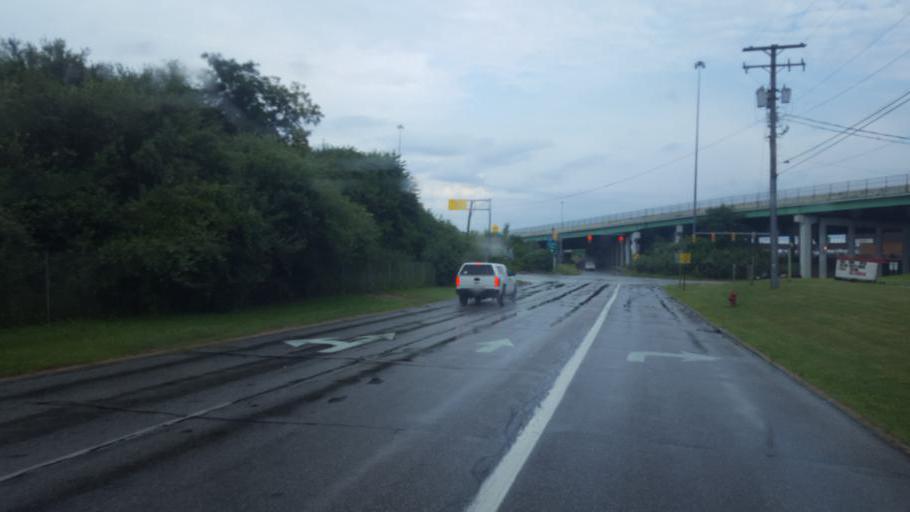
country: US
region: Ohio
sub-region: Cuyahoga County
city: Bedford Heights
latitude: 41.4230
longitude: -81.5265
